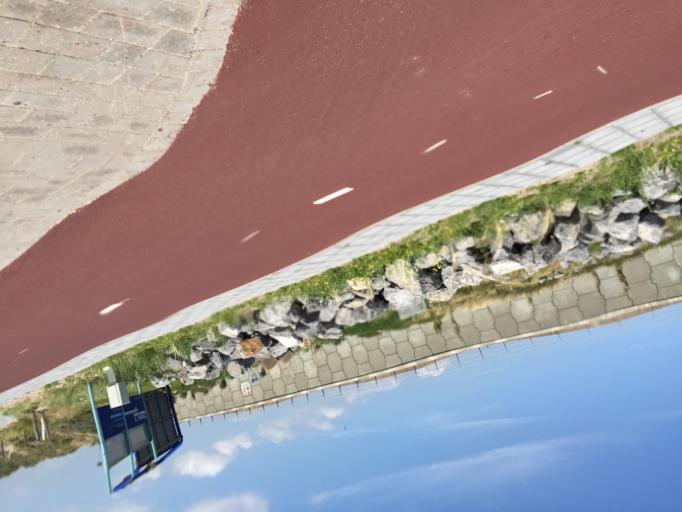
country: NL
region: North Holland
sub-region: Gemeente Bloemendaal
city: Bloemendaal
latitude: 52.4573
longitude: 4.5689
